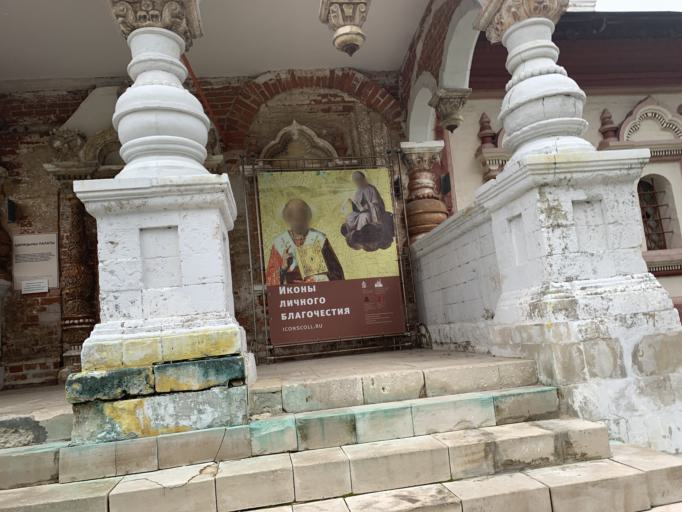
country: RU
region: Moskovskaya
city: Zvenigorod
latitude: 55.7282
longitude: 36.8165
